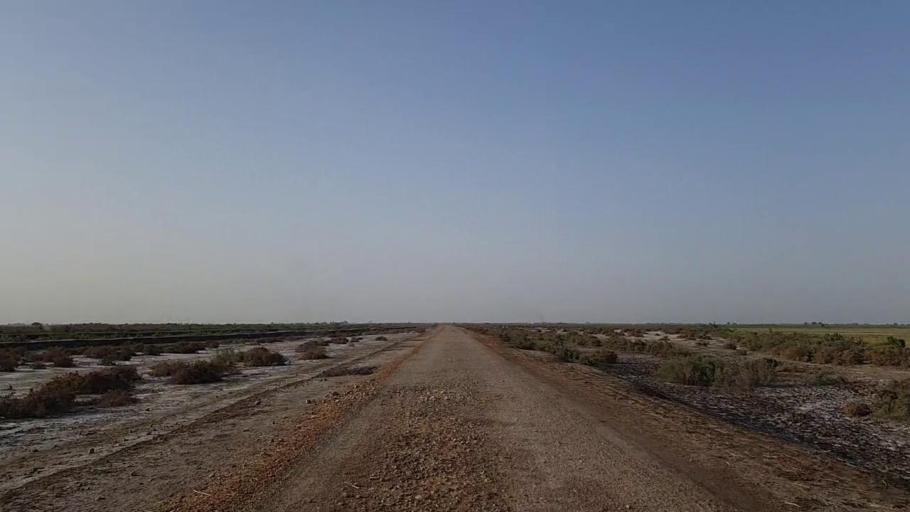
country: PK
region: Sindh
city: Jati
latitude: 24.3531
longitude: 68.1488
